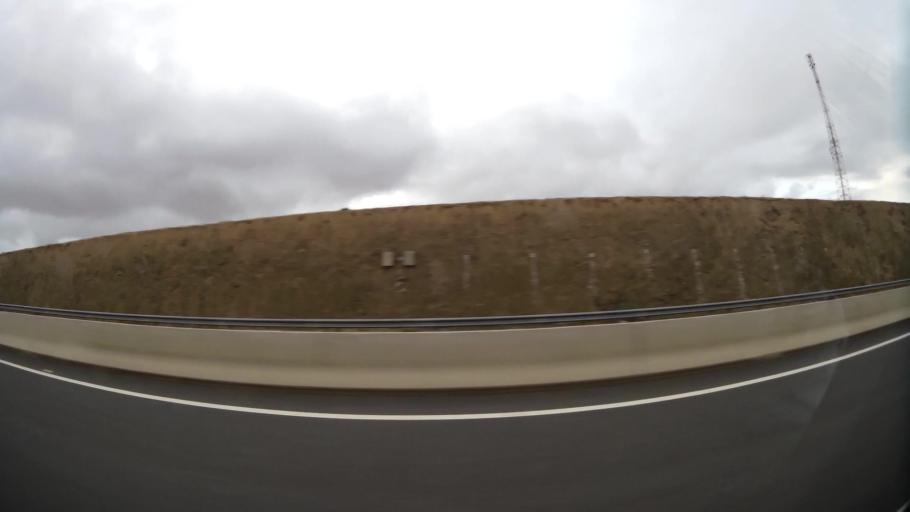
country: MA
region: Taza-Al Hoceima-Taounate
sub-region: Taza
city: Guercif
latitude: 34.3857
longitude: -3.2281
